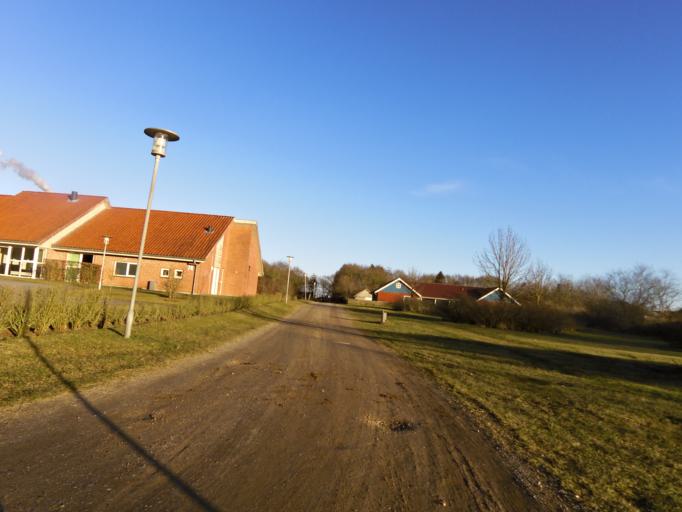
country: DK
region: South Denmark
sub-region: Esbjerg Kommune
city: Ribe
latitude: 55.3410
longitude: 8.7872
